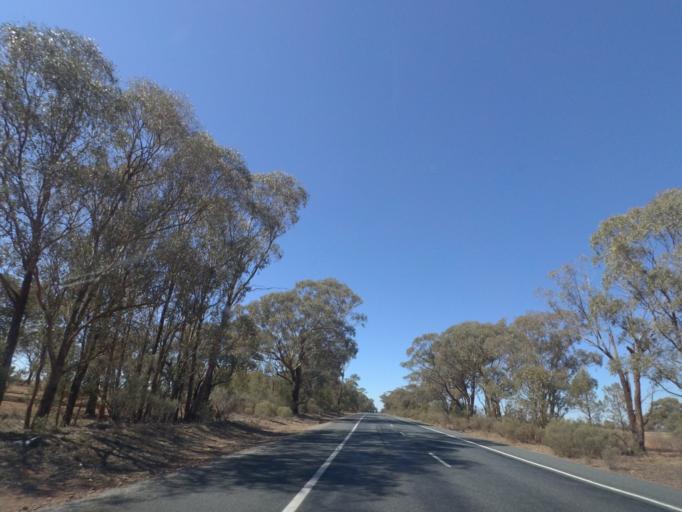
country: AU
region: New South Wales
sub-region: Bland
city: West Wyalong
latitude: -34.2096
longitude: 147.1089
